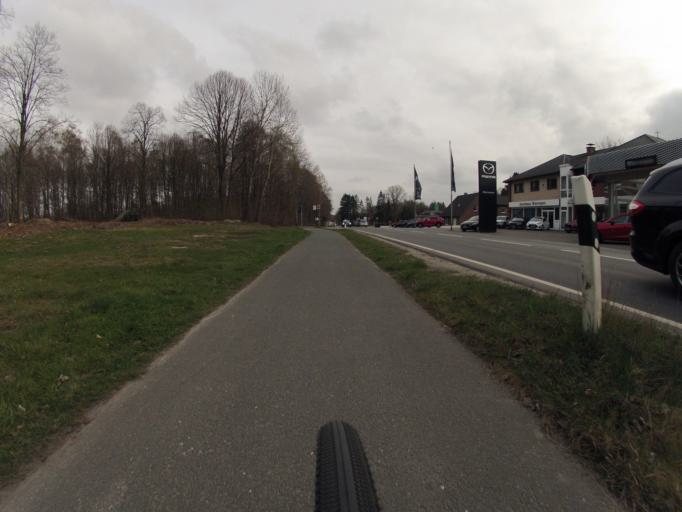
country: DE
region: North Rhine-Westphalia
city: Ibbenburen
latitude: 52.3008
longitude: 7.6916
